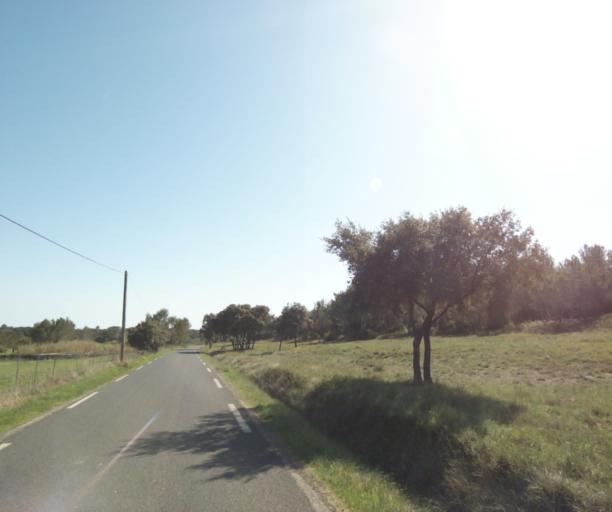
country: FR
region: Languedoc-Roussillon
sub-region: Departement de l'Herault
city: Castries
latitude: 43.7013
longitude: 3.9620
